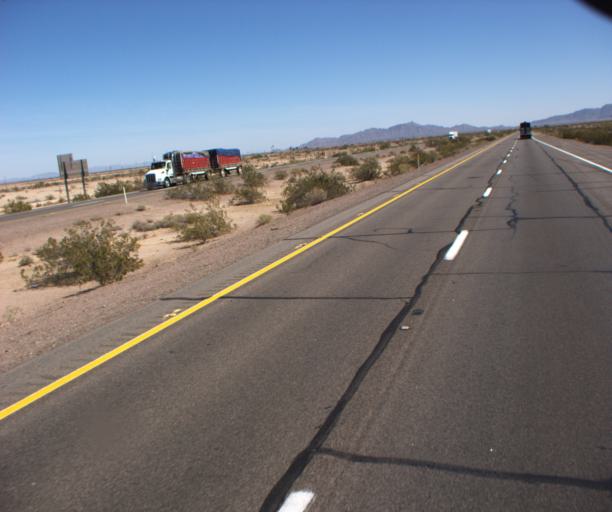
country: US
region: Arizona
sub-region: Yuma County
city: Wellton
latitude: 32.6943
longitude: -113.9472
